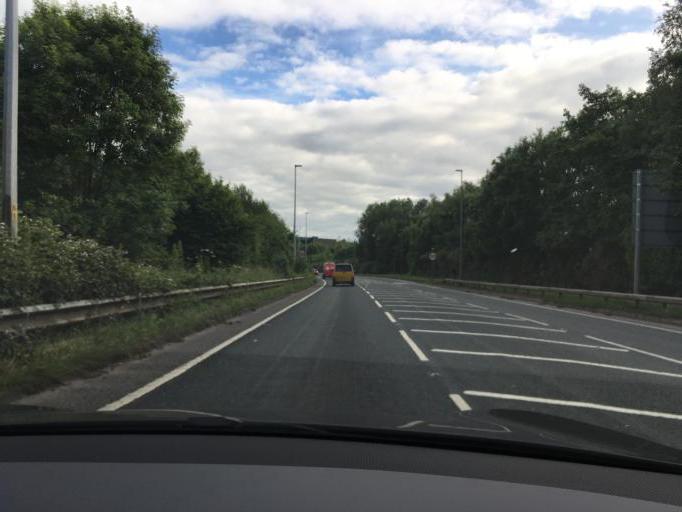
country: GB
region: England
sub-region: City and Borough of Salford
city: Irlam
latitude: 53.4419
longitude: -2.4128
